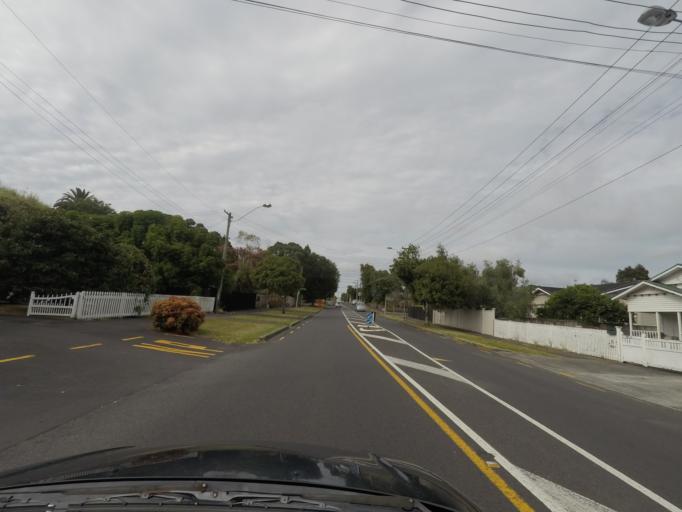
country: NZ
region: Auckland
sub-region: Auckland
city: Rosebank
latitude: -36.8840
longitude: 174.7103
